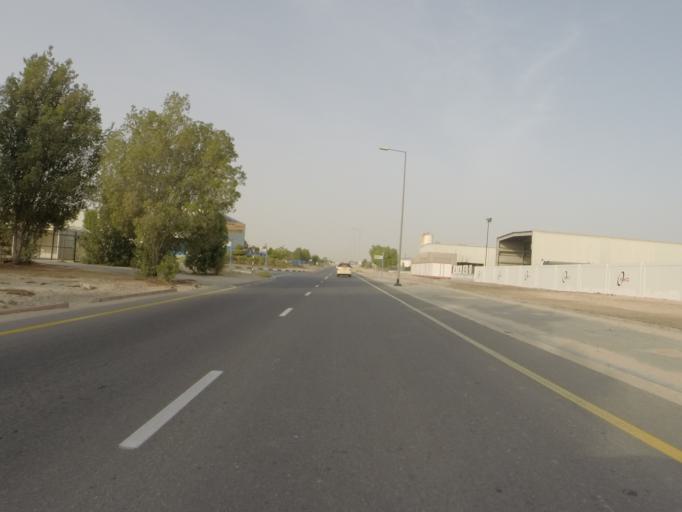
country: AE
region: Dubai
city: Dubai
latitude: 24.9648
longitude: 55.0748
